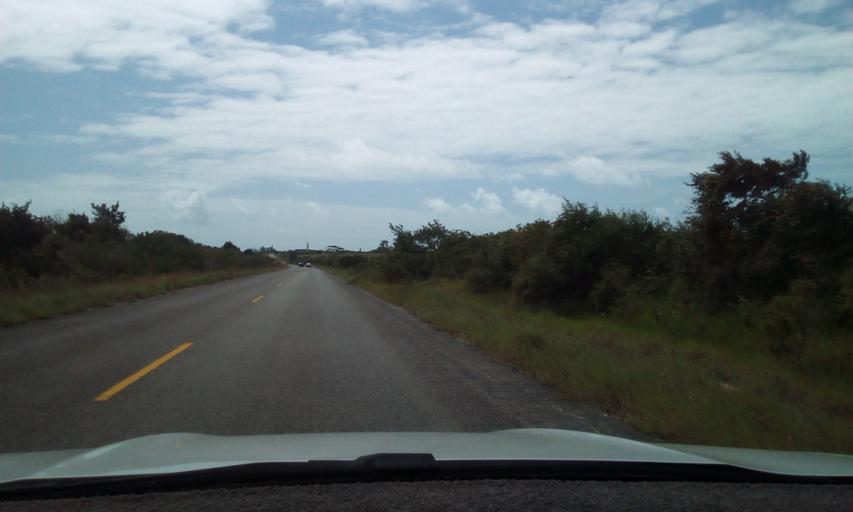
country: BR
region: Paraiba
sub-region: Rio Tinto
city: Rio Tinto
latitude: -6.7383
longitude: -34.9644
